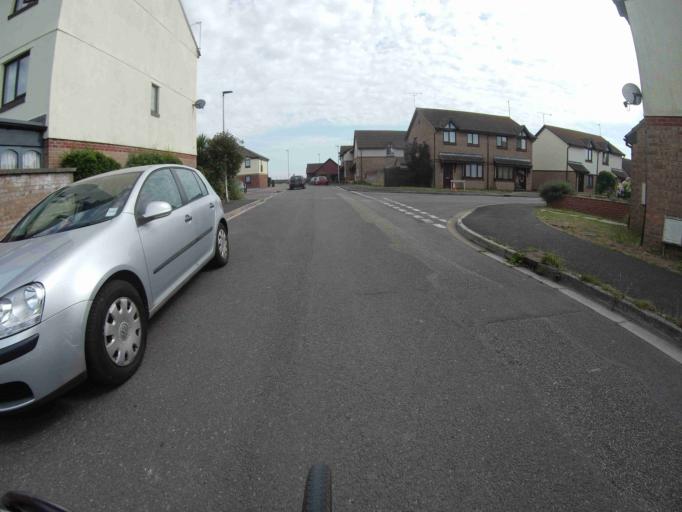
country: GB
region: England
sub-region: Devon
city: Starcross
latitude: 50.6250
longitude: -3.4474
